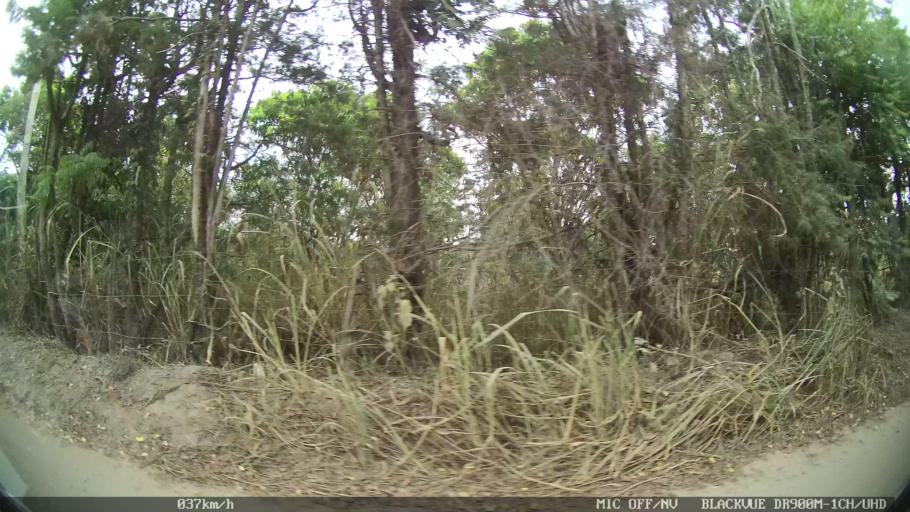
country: BR
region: Sao Paulo
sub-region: Americana
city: Americana
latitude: -22.6698
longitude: -47.3744
